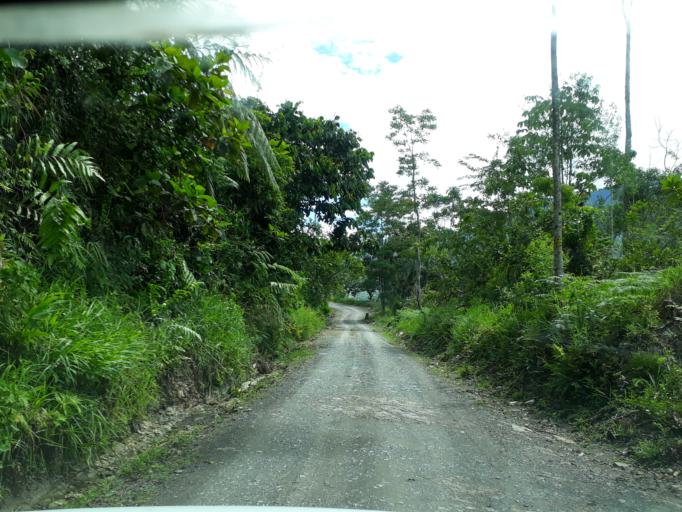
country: CO
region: Boyaca
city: Quipama
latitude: 5.4356
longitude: -74.1845
